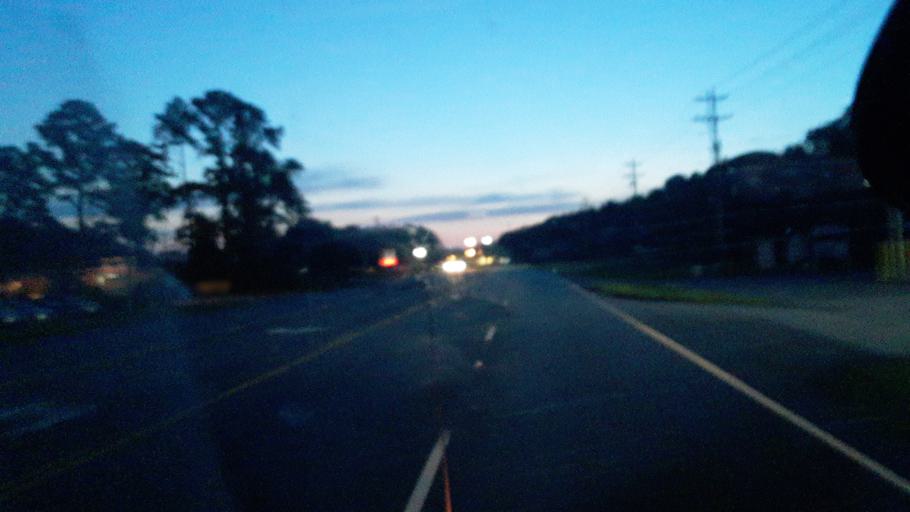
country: US
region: South Carolina
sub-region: Horry County
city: Little River
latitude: 33.8781
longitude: -78.6097
